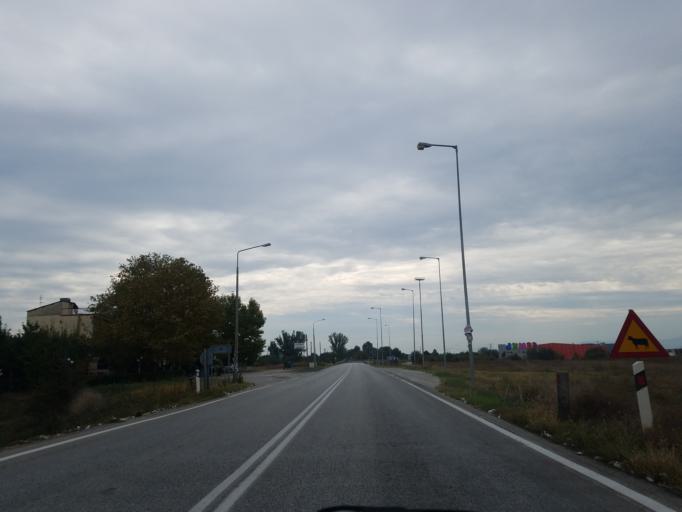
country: GR
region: Thessaly
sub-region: Nomos Kardhitsas
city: Agnantero
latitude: 39.4792
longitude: 21.8429
